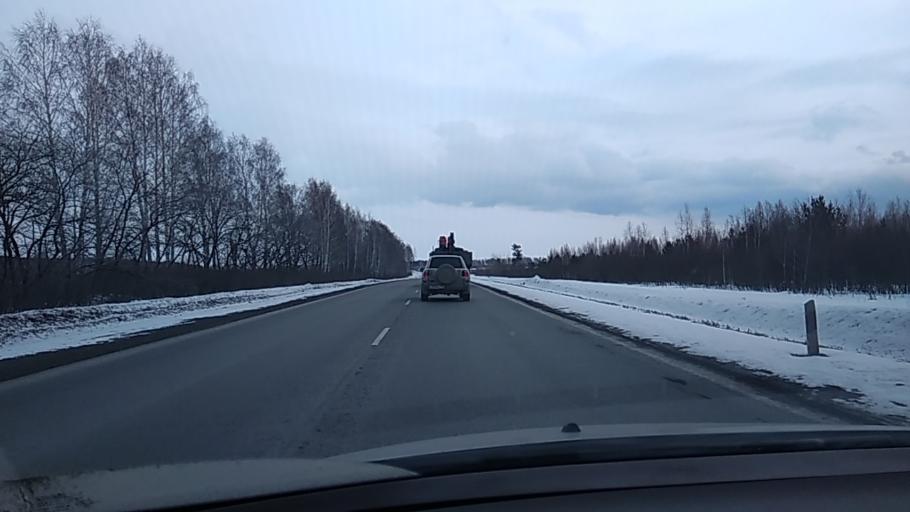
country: RU
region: Sverdlovsk
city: Sovkhoznyy
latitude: 56.5117
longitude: 61.4568
